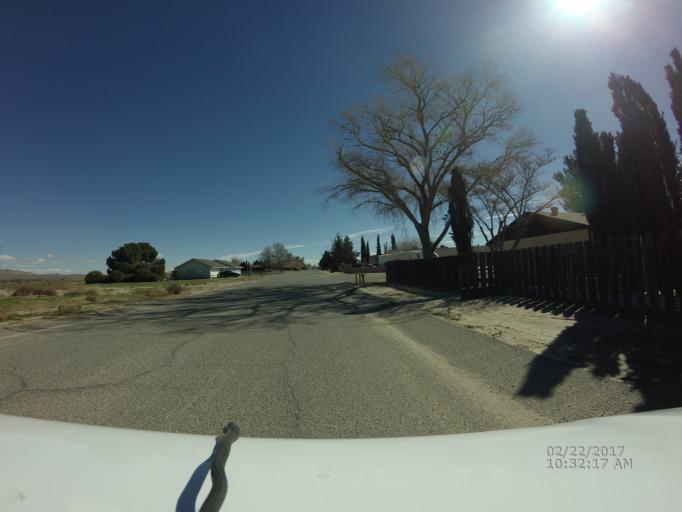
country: US
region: California
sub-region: Los Angeles County
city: Lake Los Angeles
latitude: 34.6303
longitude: -117.8242
